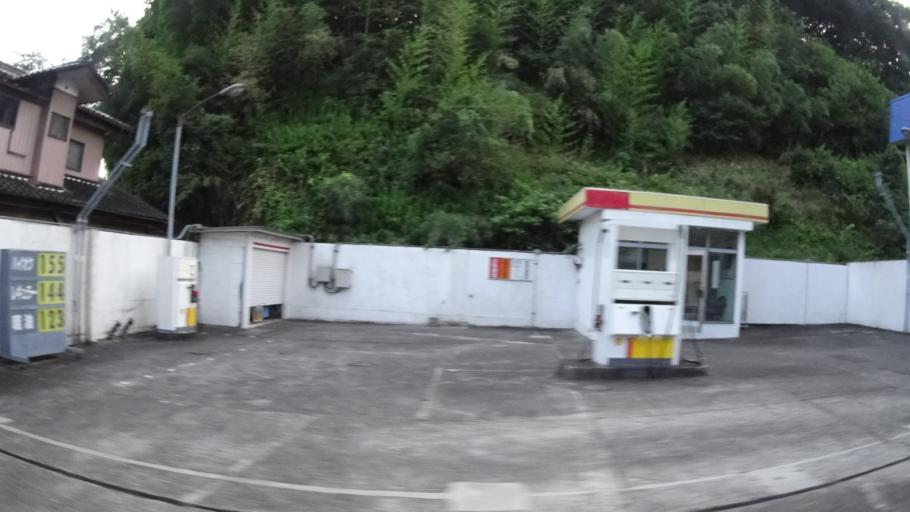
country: JP
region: Tochigi
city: Karasuyama
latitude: 36.6016
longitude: 140.1510
